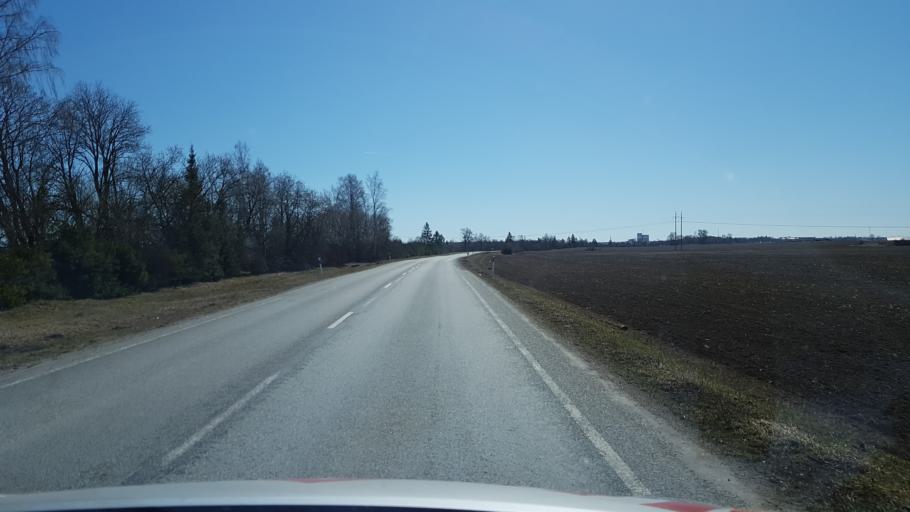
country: EE
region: Laeaene-Virumaa
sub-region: Someru vald
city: Someru
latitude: 59.3837
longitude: 26.3930
